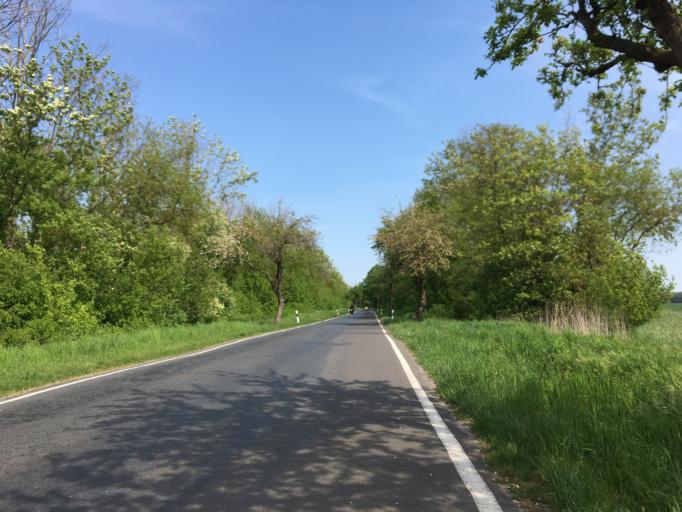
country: DE
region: Brandenburg
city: Werneuchen
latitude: 52.6553
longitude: 13.7300
